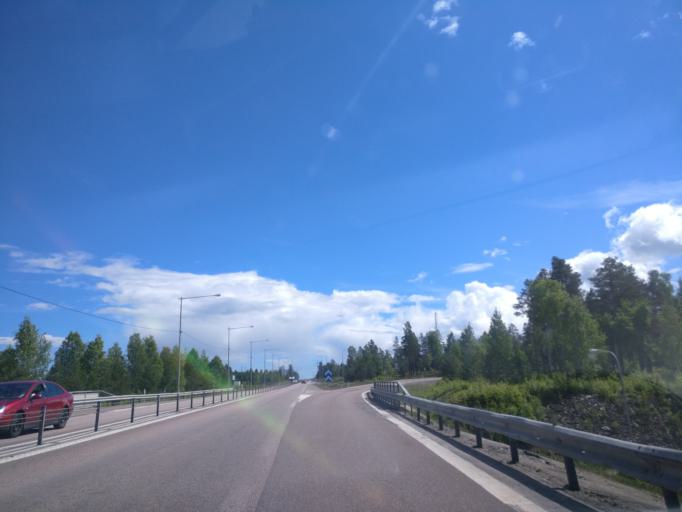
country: SE
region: Vaesternorrland
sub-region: Haernoesands Kommun
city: Haernoesand
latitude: 62.6537
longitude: 17.8832
